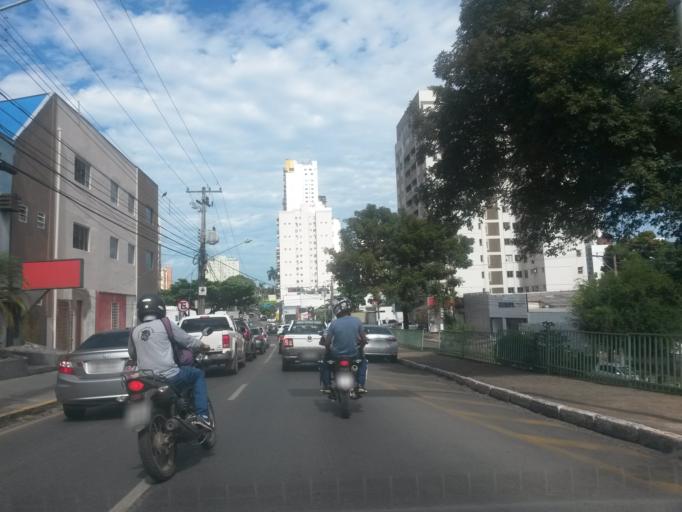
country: BR
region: Mato Grosso
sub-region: Cuiaba
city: Cuiaba
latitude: -15.5868
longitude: -56.0976
